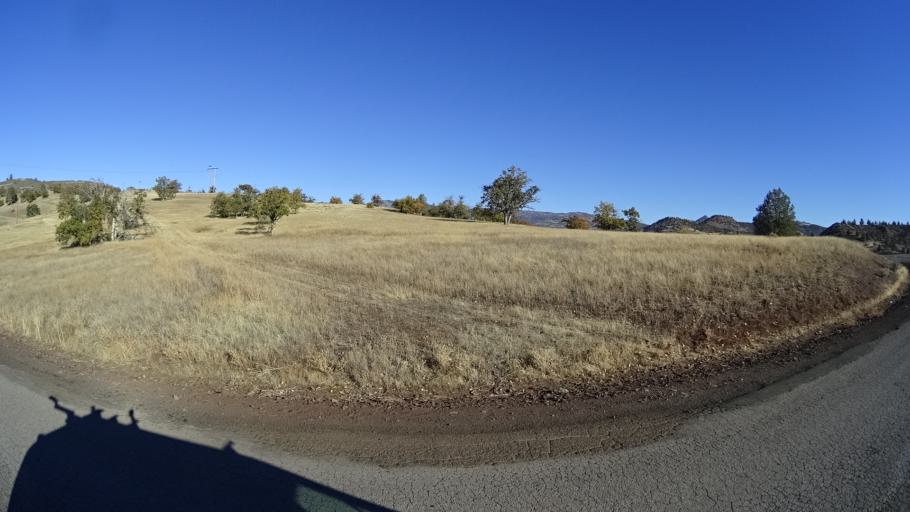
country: US
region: California
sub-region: Siskiyou County
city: Montague
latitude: 41.9503
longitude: -122.4374
